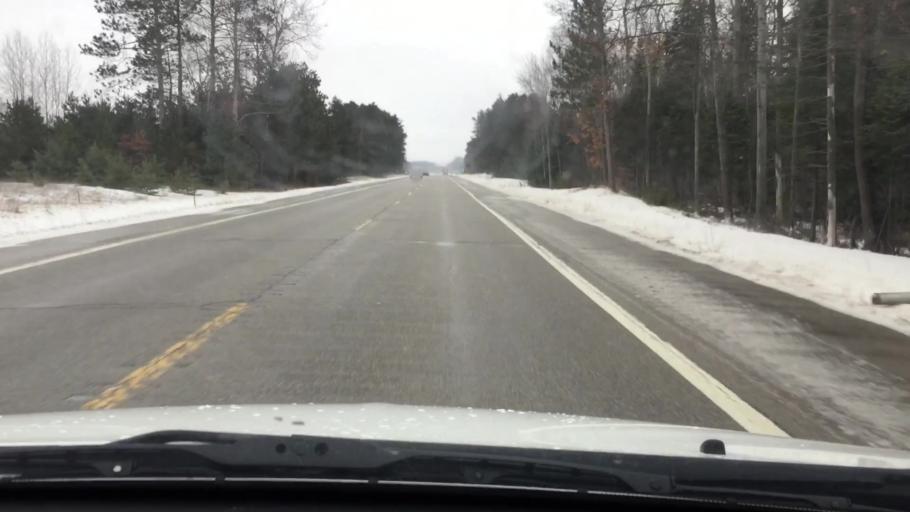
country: US
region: Michigan
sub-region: Wexford County
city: Cadillac
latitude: 44.2107
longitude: -85.4208
